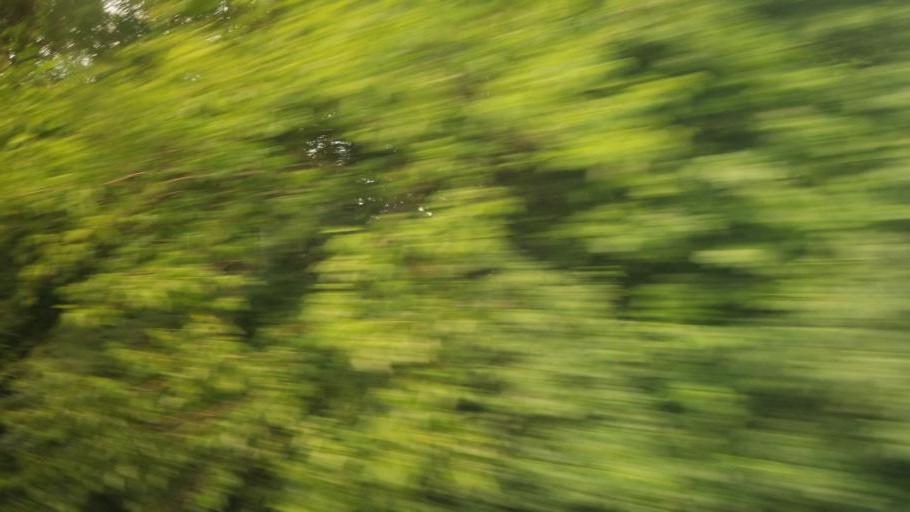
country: US
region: Illinois
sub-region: Cook County
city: Western Springs
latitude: 41.8127
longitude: -87.8847
